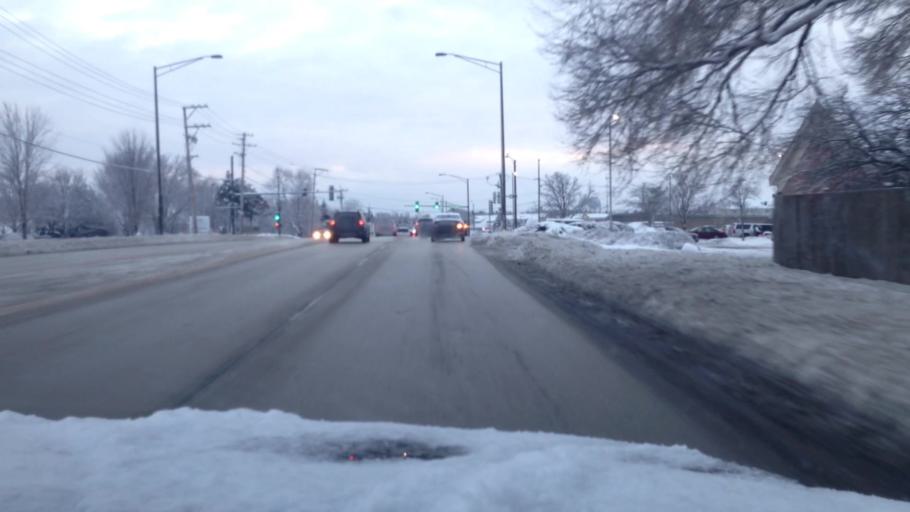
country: US
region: Illinois
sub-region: Kane County
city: South Elgin
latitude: 42.0083
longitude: -88.3151
